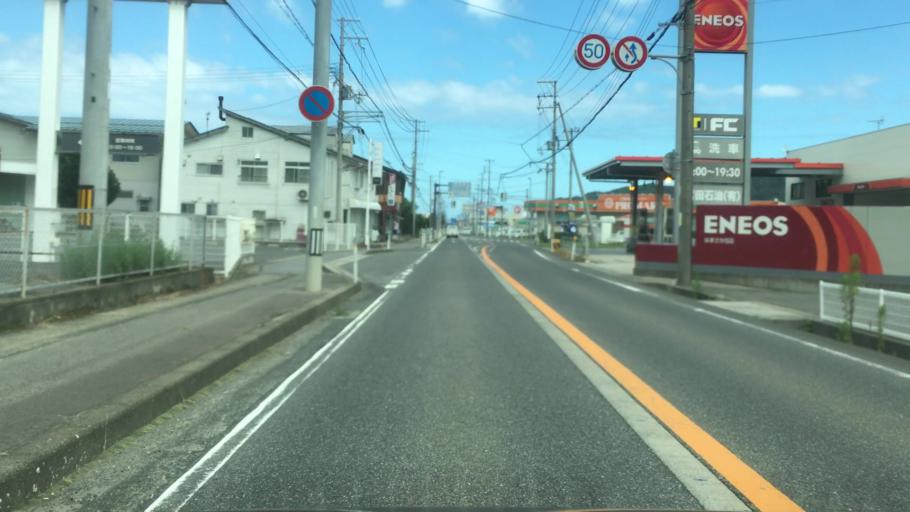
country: JP
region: Tottori
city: Tottori
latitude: 35.6137
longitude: 134.4671
